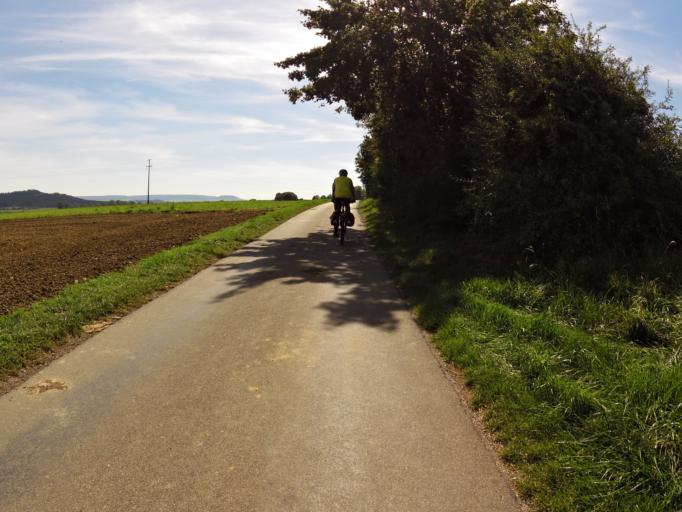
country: DE
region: Baden-Wuerttemberg
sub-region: Freiburg Region
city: Bad Durrheim
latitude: 48.0037
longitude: 8.5027
